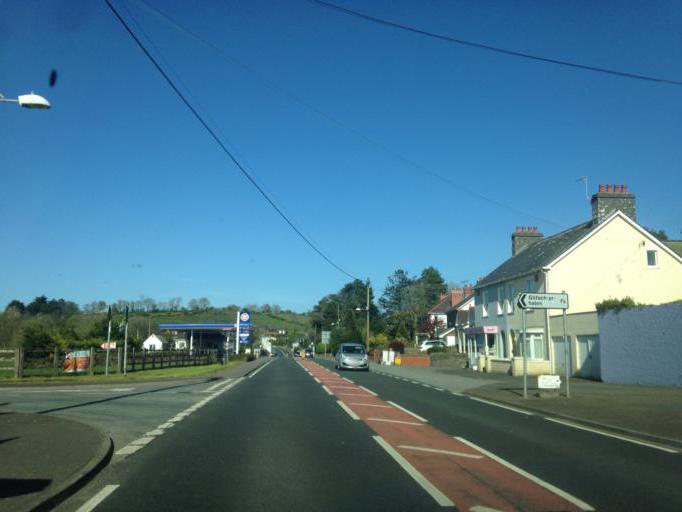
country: GB
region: Wales
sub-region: County of Ceredigion
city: Llanarth
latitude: 52.2125
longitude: -4.2833
